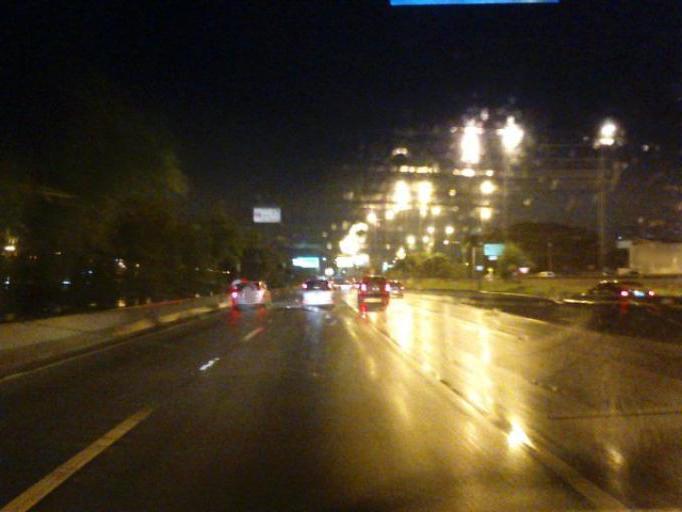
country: BR
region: Sao Paulo
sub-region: Sao Paulo
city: Sao Paulo
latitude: -23.5088
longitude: -46.6938
